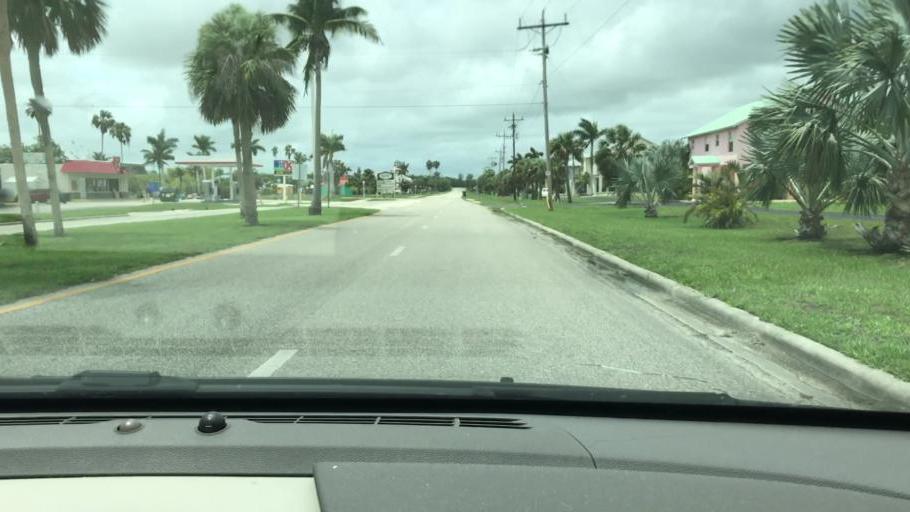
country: US
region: Florida
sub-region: Collier County
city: Marco
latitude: 25.8652
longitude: -81.3826
